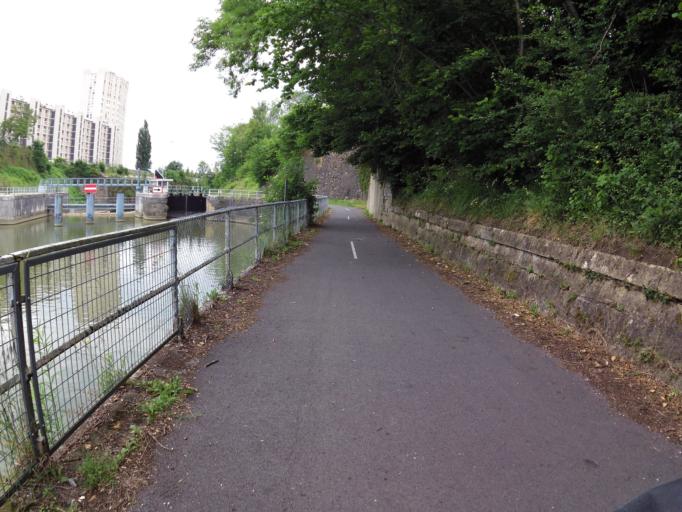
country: FR
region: Champagne-Ardenne
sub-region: Departement des Ardennes
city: Charleville-Mezieres
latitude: 49.7602
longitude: 4.7248
